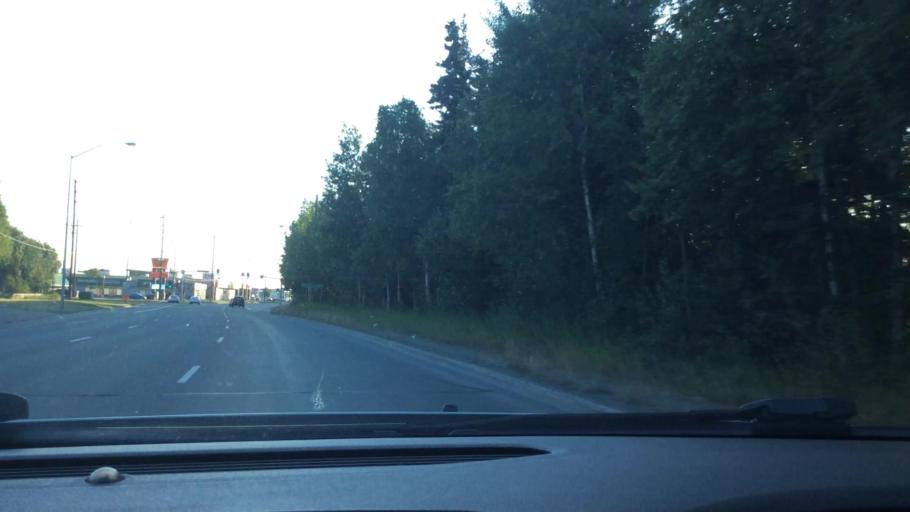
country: US
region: Alaska
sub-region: Anchorage Municipality
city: Anchorage
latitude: 61.1955
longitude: -149.8572
